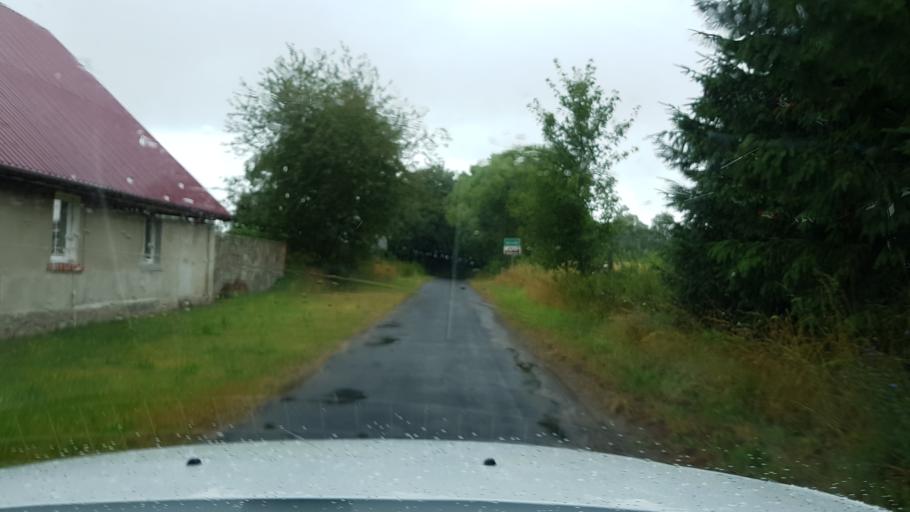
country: PL
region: West Pomeranian Voivodeship
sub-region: Powiat mysliborski
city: Barlinek
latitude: 52.9906
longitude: 15.1226
